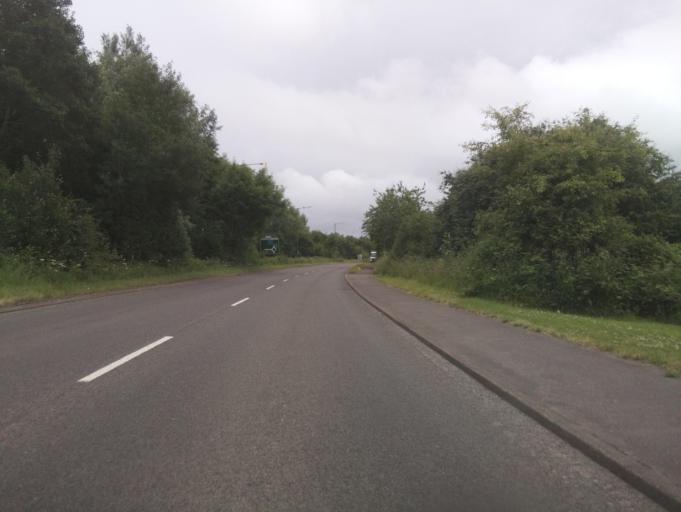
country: GB
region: England
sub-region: Derbyshire
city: Rodsley
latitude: 52.8782
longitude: -1.6991
